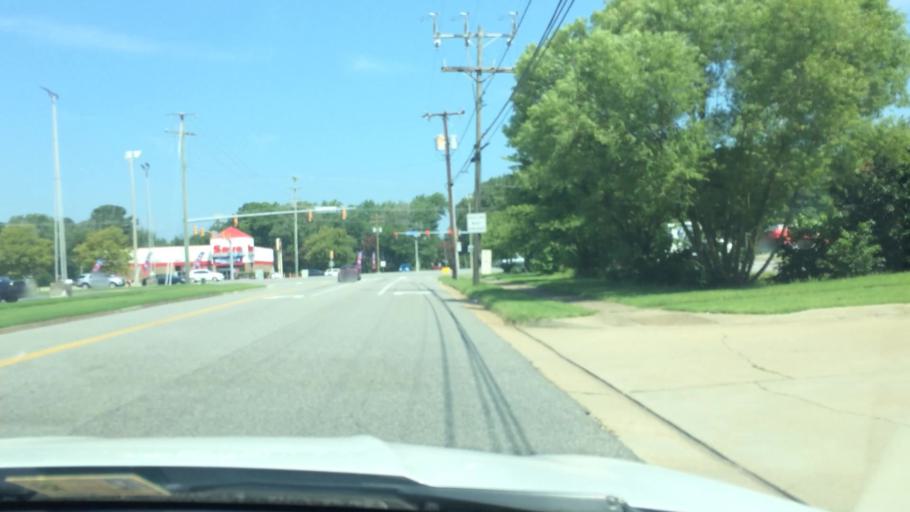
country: US
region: Virginia
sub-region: City of Newport News
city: Newport News
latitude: 37.0240
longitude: -76.4330
